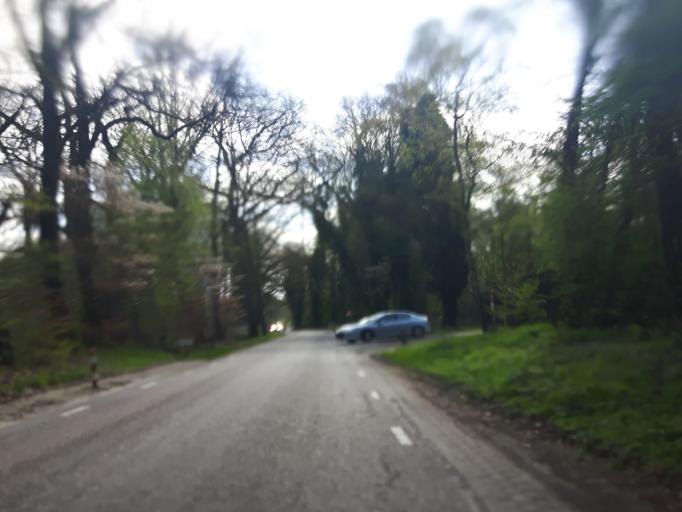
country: NL
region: Overijssel
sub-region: Gemeente Enschede
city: Enschede
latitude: 52.1939
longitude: 6.8306
